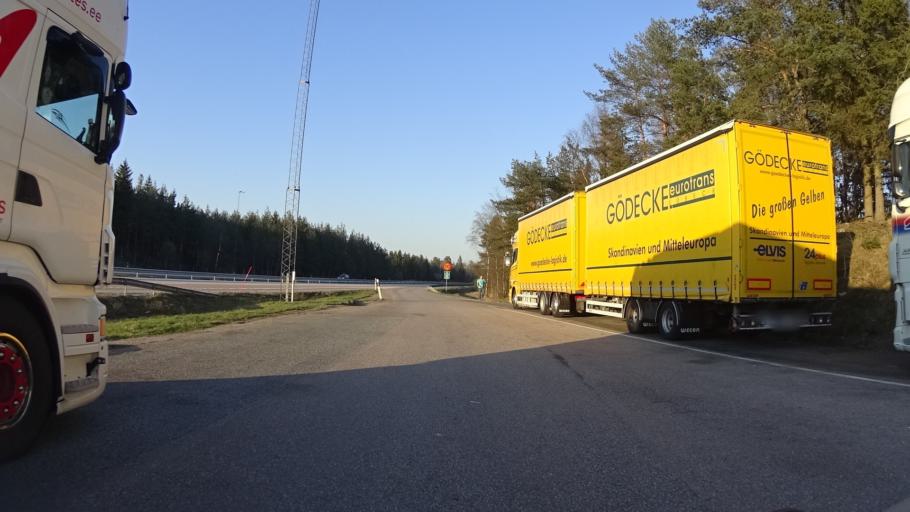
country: SE
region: Stockholm
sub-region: Sodertalje Kommun
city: Molnbo
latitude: 58.9176
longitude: 17.3702
